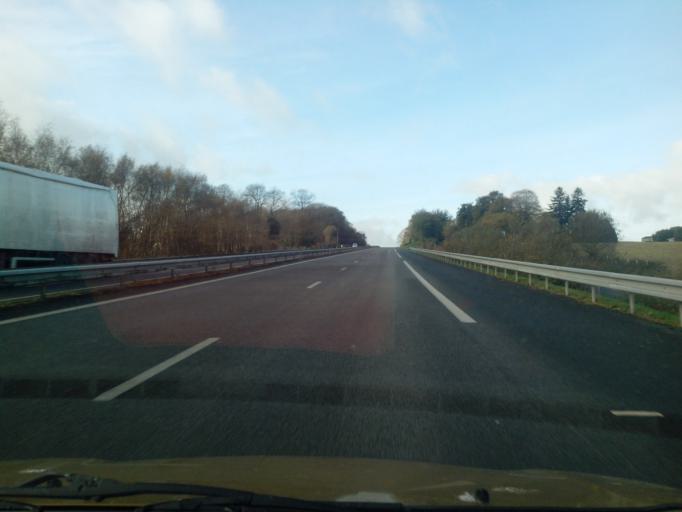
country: FR
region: Brittany
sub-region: Departement du Morbihan
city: Bignan
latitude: 47.9058
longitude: -2.7732
